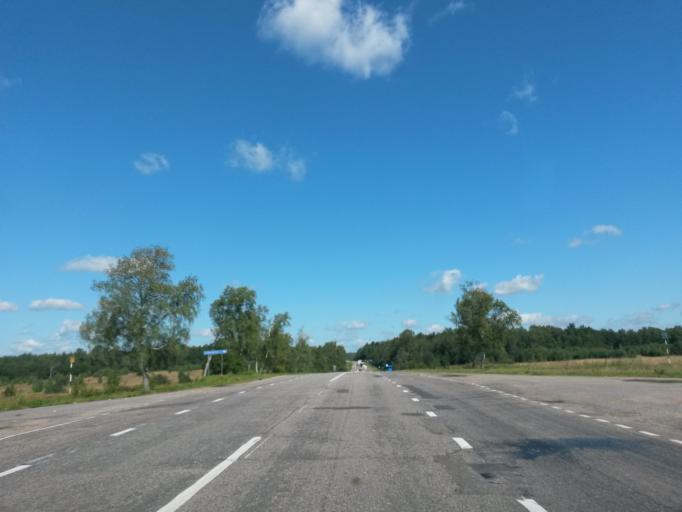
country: RU
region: Jaroslavl
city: Gavrilov-Yam
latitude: 57.4470
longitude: 39.9148
